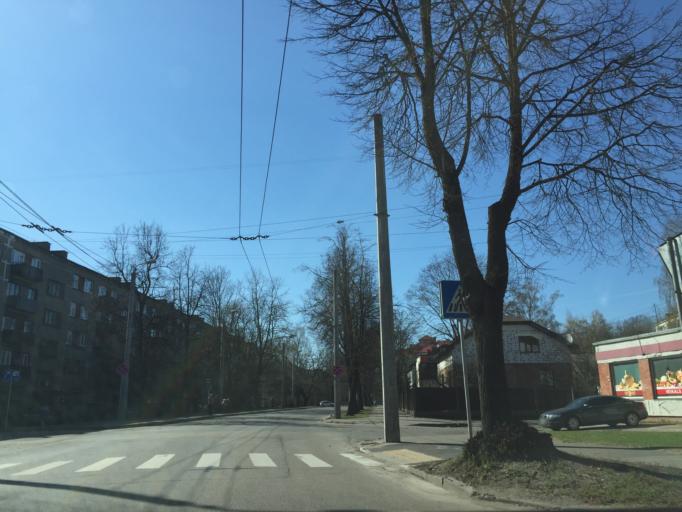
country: LV
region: Riga
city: Riga
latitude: 56.9160
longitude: 24.0941
